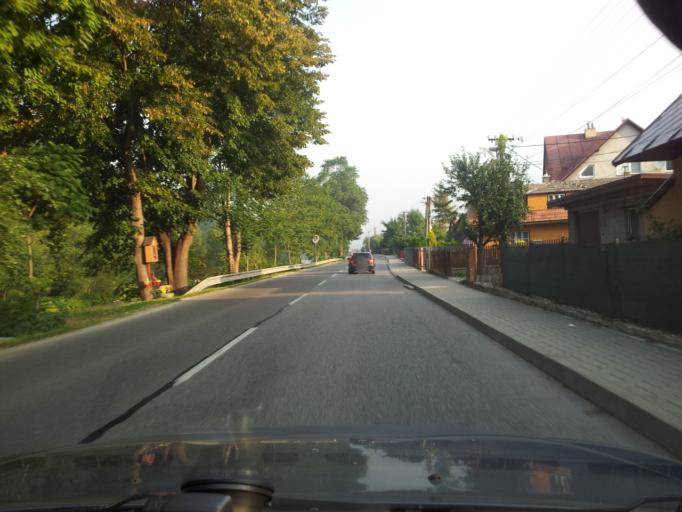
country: SK
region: Zilinsky
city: Cadca
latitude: 49.3720
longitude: 18.8947
